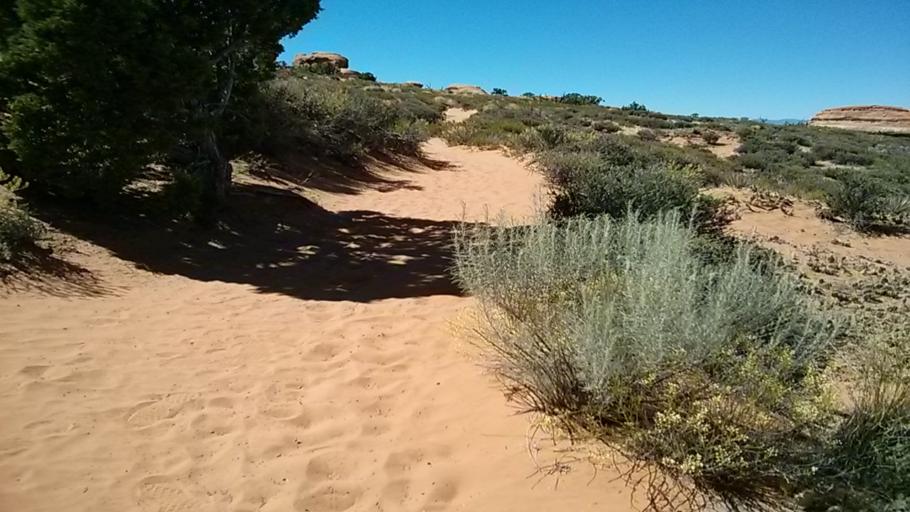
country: US
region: Utah
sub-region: Grand County
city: Moab
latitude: 38.7928
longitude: -109.6053
